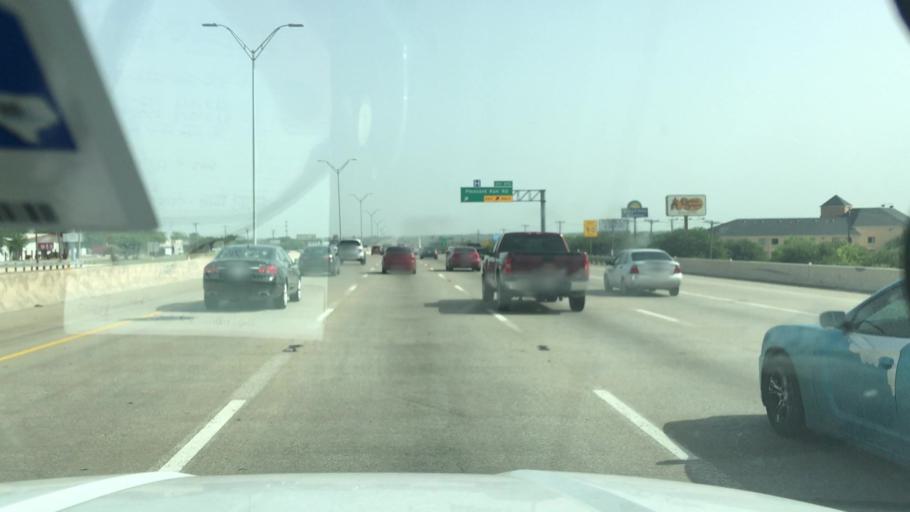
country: US
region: Texas
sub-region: Dallas County
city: DeSoto
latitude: 32.6189
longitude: -96.8231
